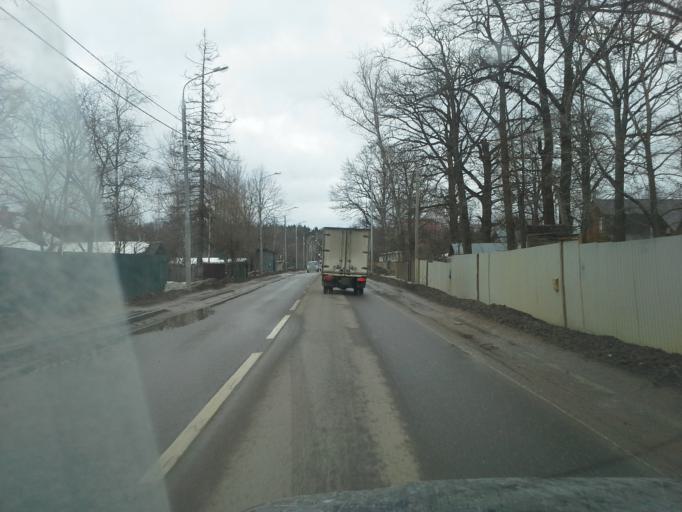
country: RU
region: Moskovskaya
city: Zhavoronki
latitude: 55.6526
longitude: 37.1008
